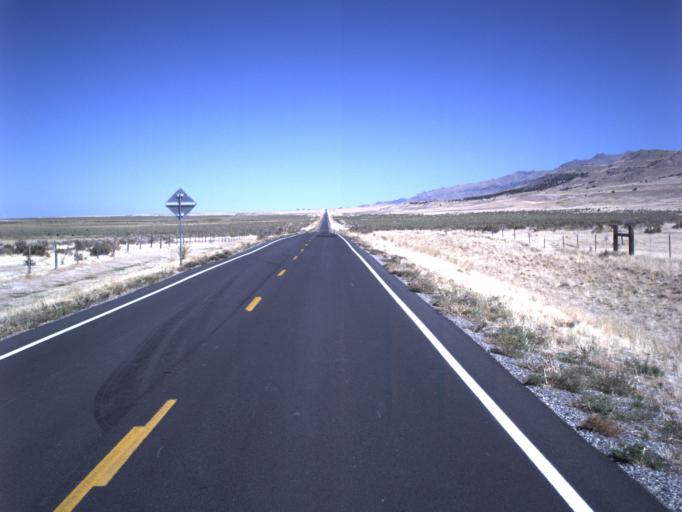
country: US
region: Utah
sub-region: Tooele County
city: Grantsville
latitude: 40.5407
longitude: -112.7453
